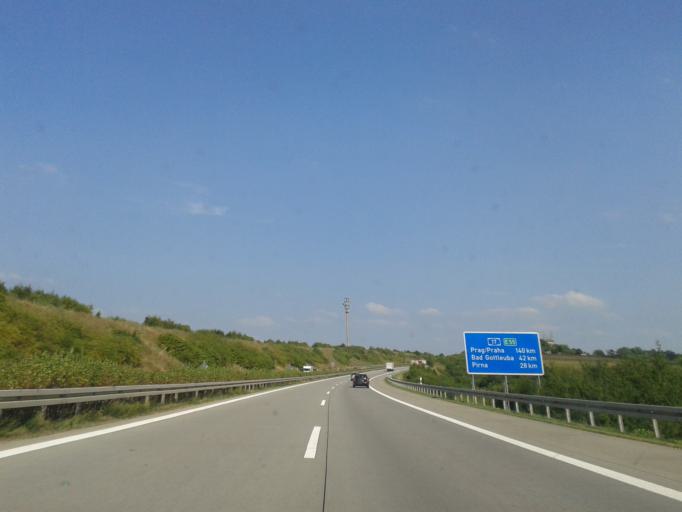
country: DE
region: Saxony
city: Freital
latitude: 51.0371
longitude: 13.6218
